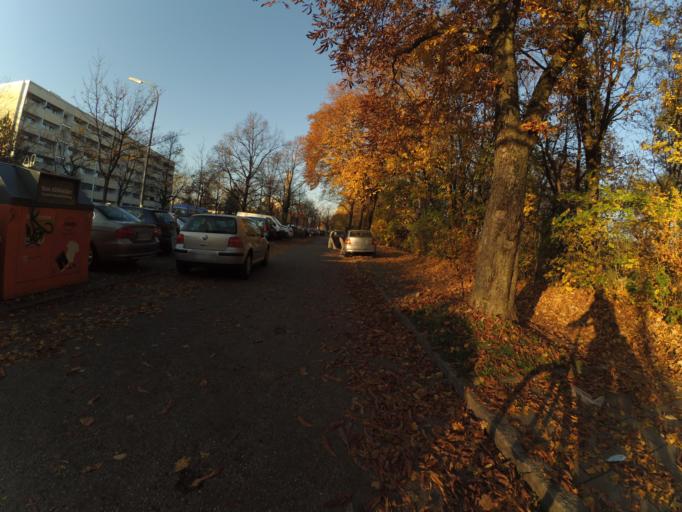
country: DE
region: Bavaria
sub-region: Upper Bavaria
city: Oberschleissheim
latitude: 48.1956
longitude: 11.5351
